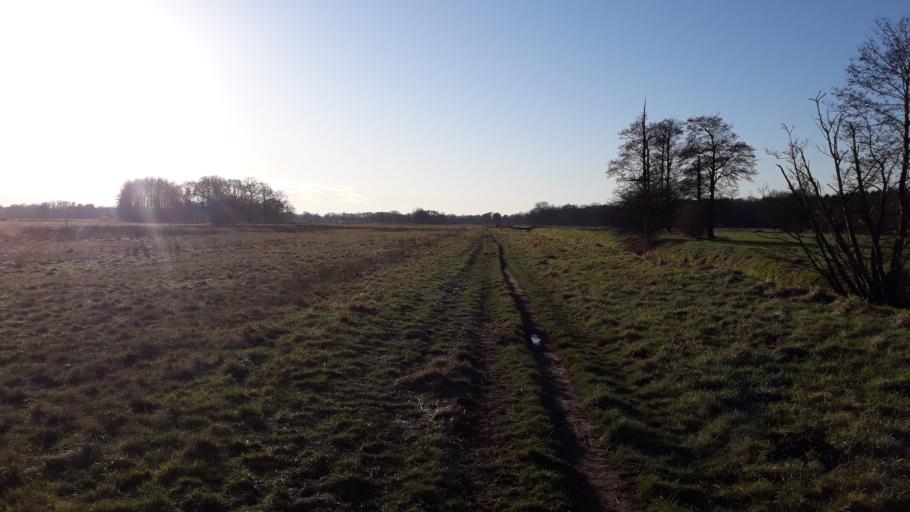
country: DE
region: Schleswig-Holstein
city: Hasloh
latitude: 53.7137
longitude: 9.8662
